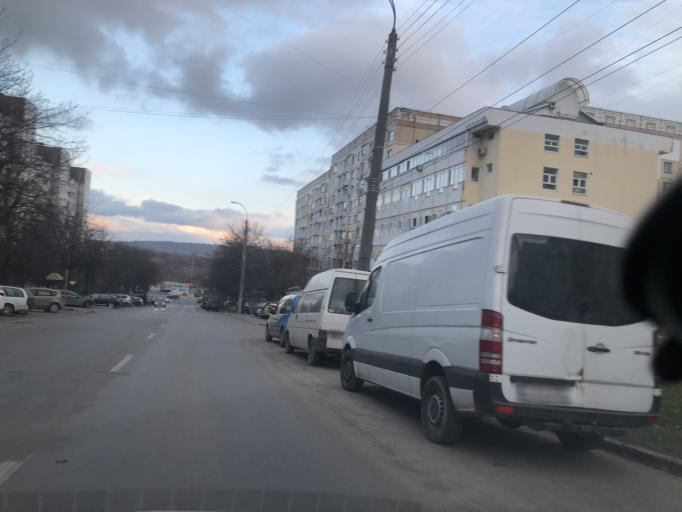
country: MD
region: Chisinau
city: Chisinau
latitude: 47.0430
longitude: 28.8952
